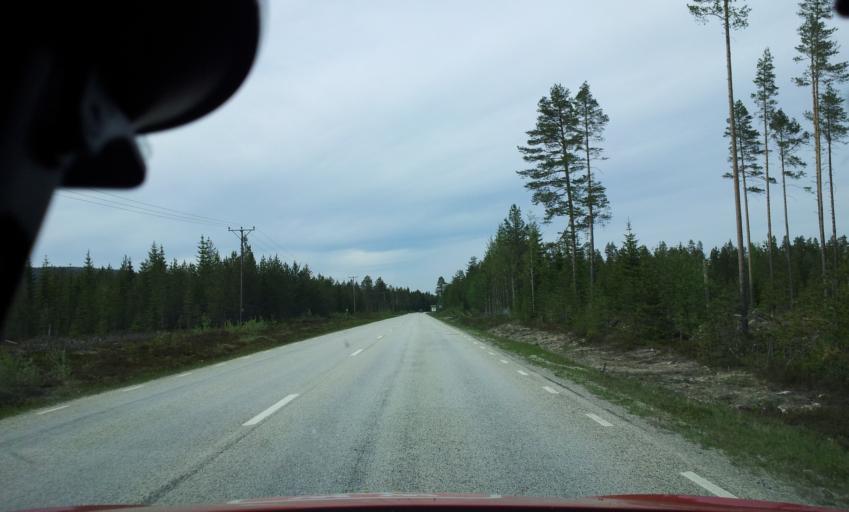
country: SE
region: Jaemtland
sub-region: Bergs Kommun
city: Hoverberg
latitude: 62.4991
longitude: 14.2073
